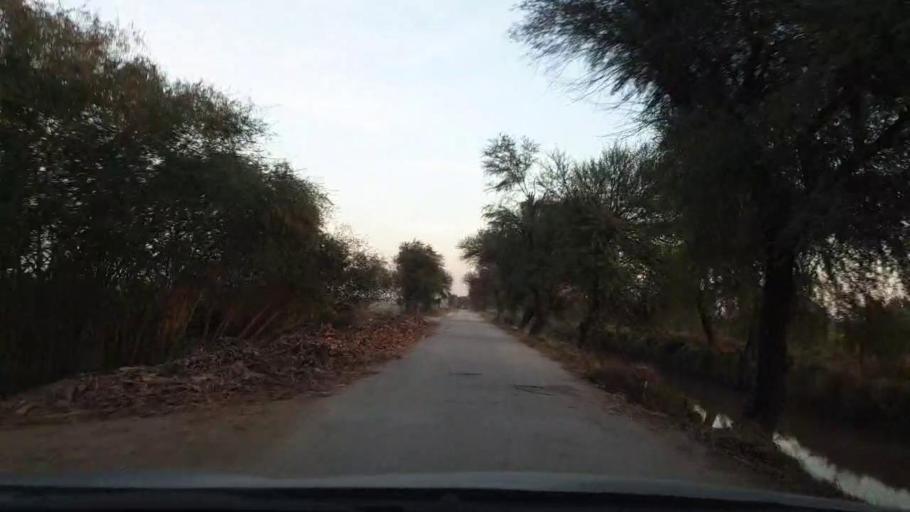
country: PK
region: Sindh
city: Tando Allahyar
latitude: 25.5913
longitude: 68.7107
